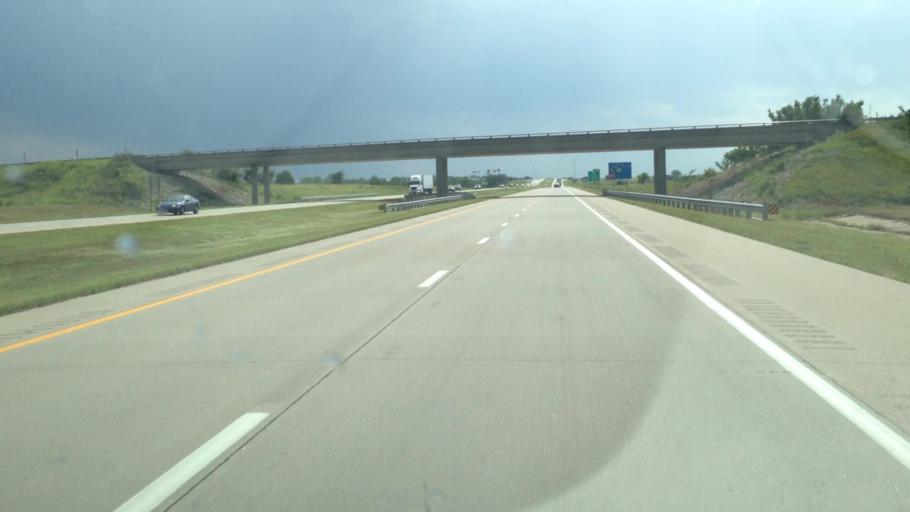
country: US
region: Kansas
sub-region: Osage County
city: Lyndon
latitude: 38.4345
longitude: -95.7091
